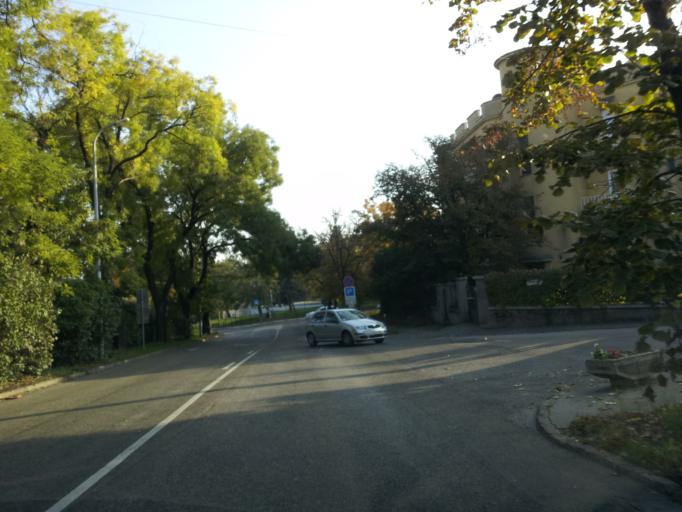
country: HU
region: Budapest
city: Budapest XII. keruelet
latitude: 47.4917
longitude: 19.0128
